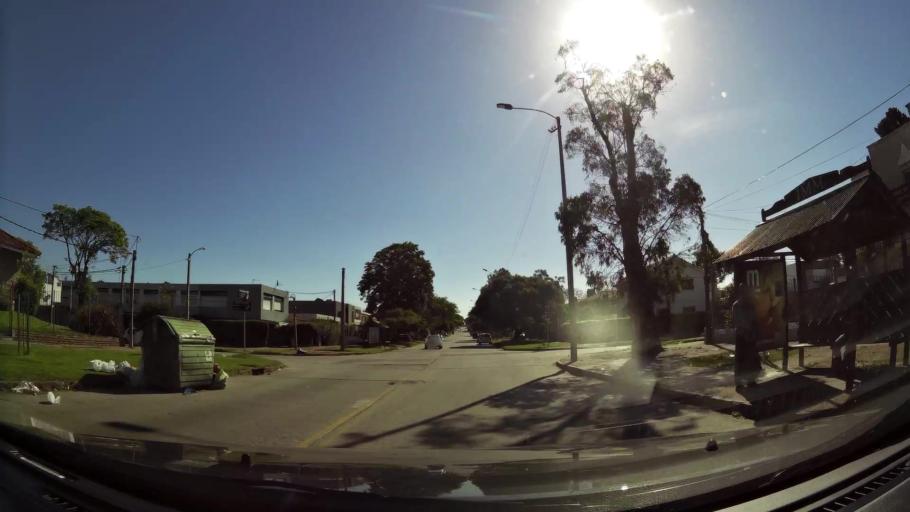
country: UY
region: Canelones
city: Paso de Carrasco
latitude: -34.8818
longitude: -56.0712
